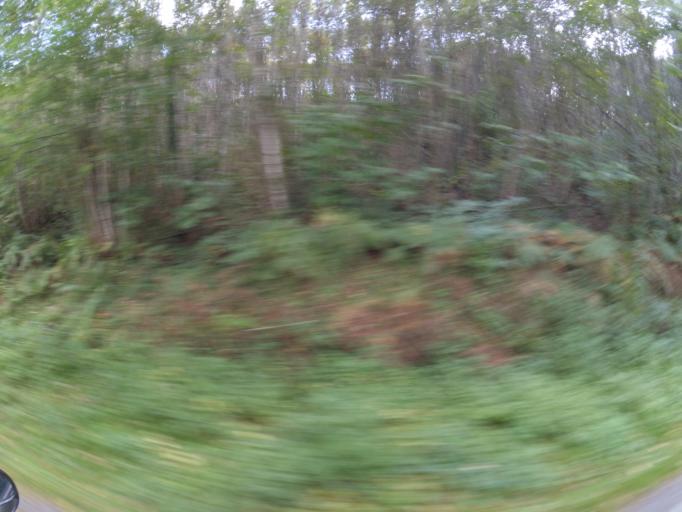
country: FR
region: Brittany
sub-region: Departement du Morbihan
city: Peillac
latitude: 47.7272
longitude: -2.2232
